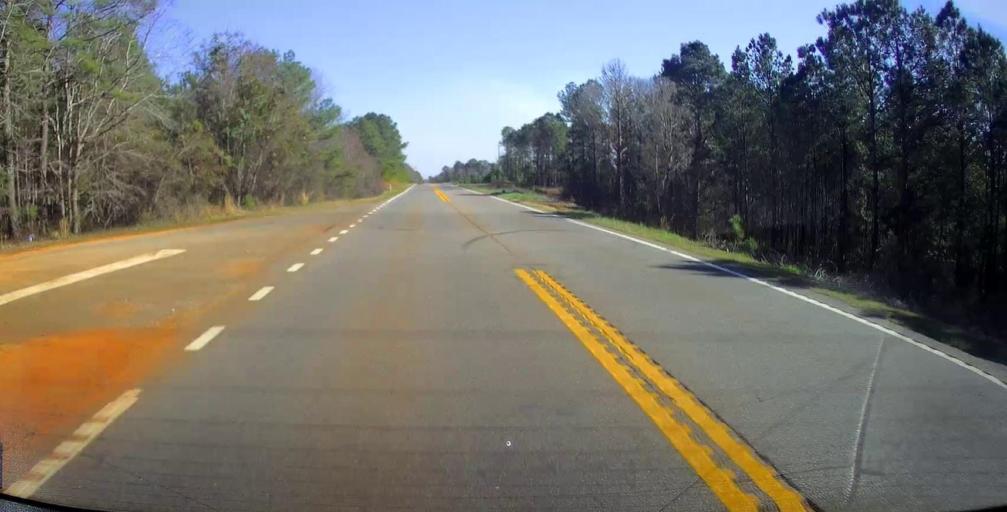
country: US
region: Georgia
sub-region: Macon County
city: Oglethorpe
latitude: 32.3587
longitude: -84.1783
